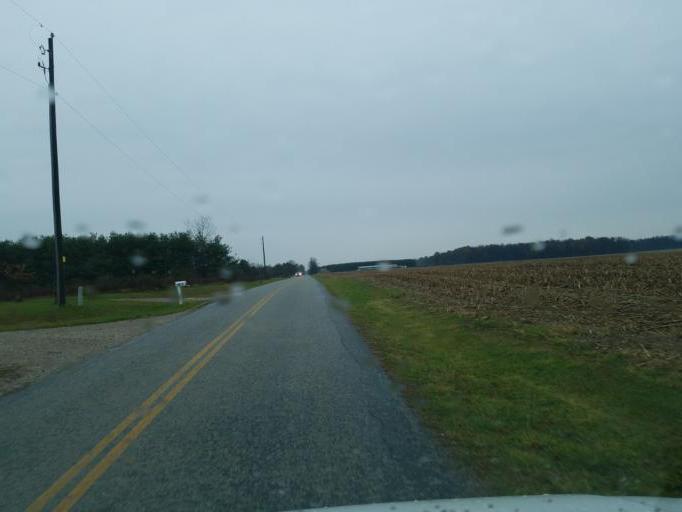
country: US
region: Ohio
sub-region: Knox County
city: Centerburg
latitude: 40.2892
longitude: -82.7736
